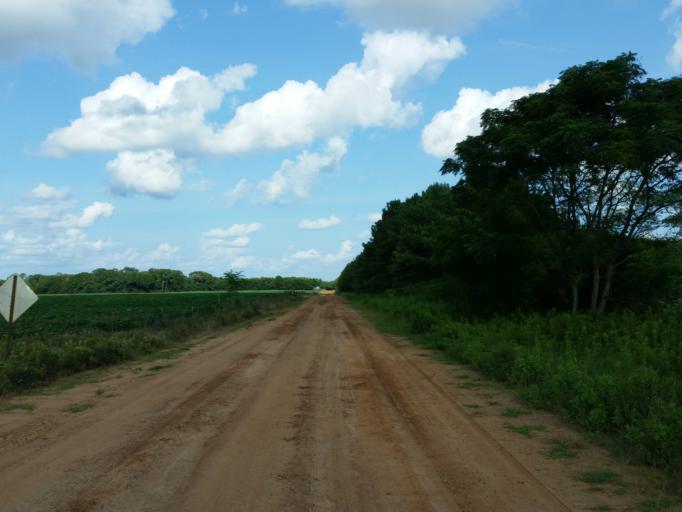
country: US
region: Georgia
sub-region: Lee County
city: Leesburg
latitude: 31.8746
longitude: -84.0624
